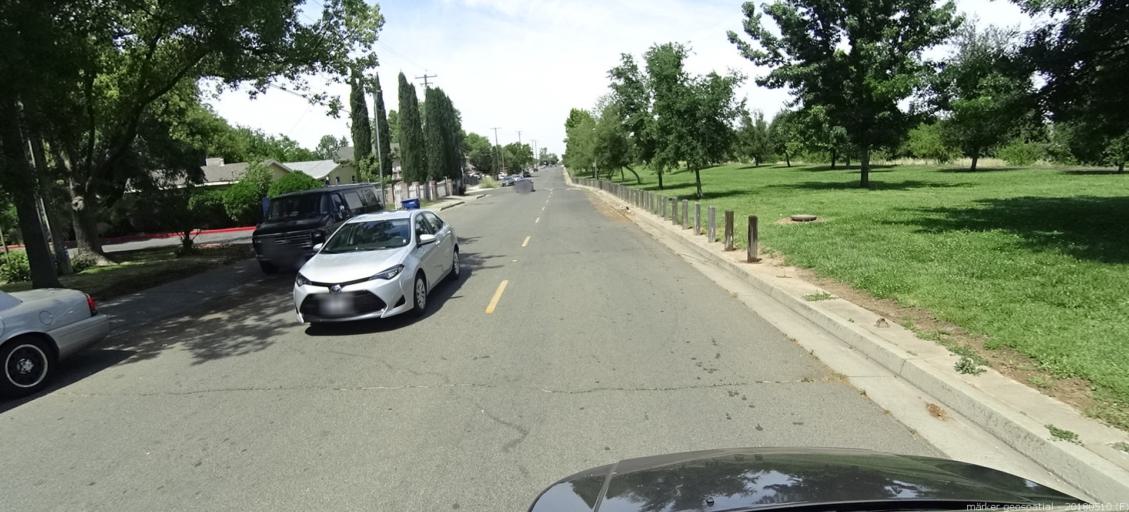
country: US
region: California
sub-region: Sacramento County
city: Rio Linda
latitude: 38.6293
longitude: -121.4479
